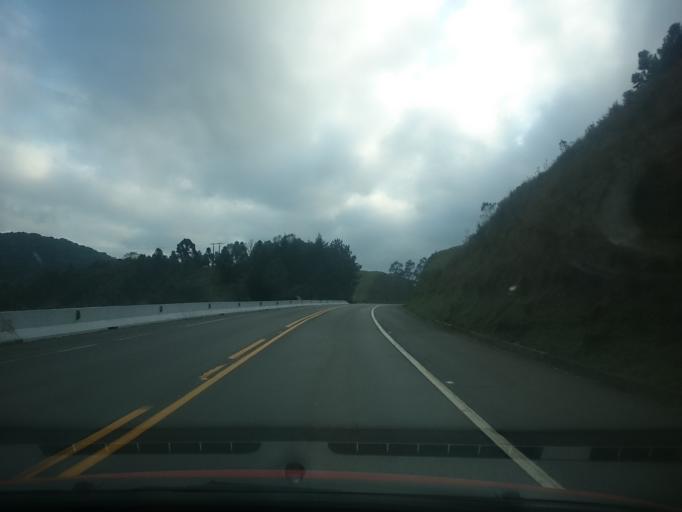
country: BR
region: Santa Catarina
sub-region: Lages
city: Lages
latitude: -27.9107
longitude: -50.4471
